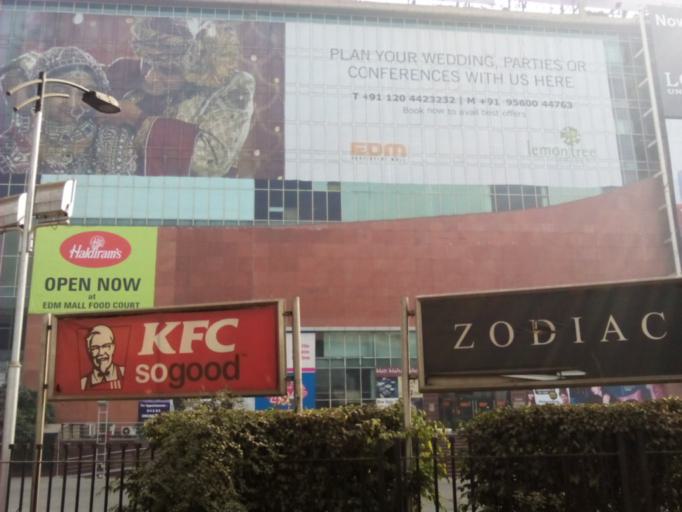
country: IN
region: Uttar Pradesh
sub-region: Gautam Buddha Nagar
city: Noida
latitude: 28.6414
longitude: 77.3161
